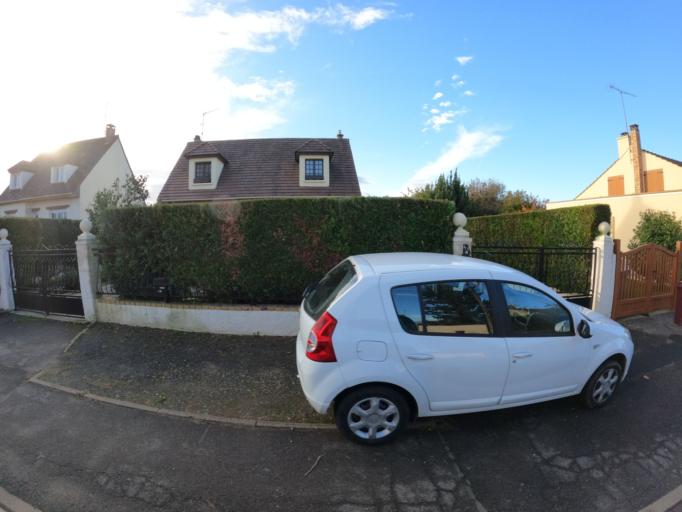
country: FR
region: Ile-de-France
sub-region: Departement de Seine-et-Marne
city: Chanteloup-en-Brie
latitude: 48.8378
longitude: 2.7584
